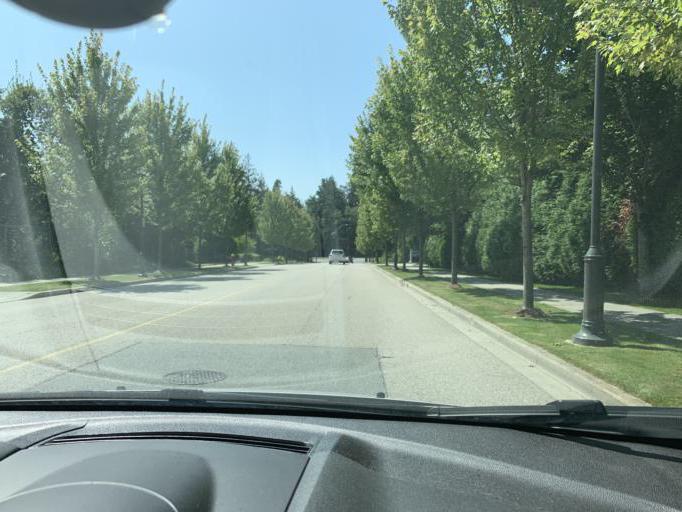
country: CA
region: British Columbia
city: West End
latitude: 49.2464
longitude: -123.2324
